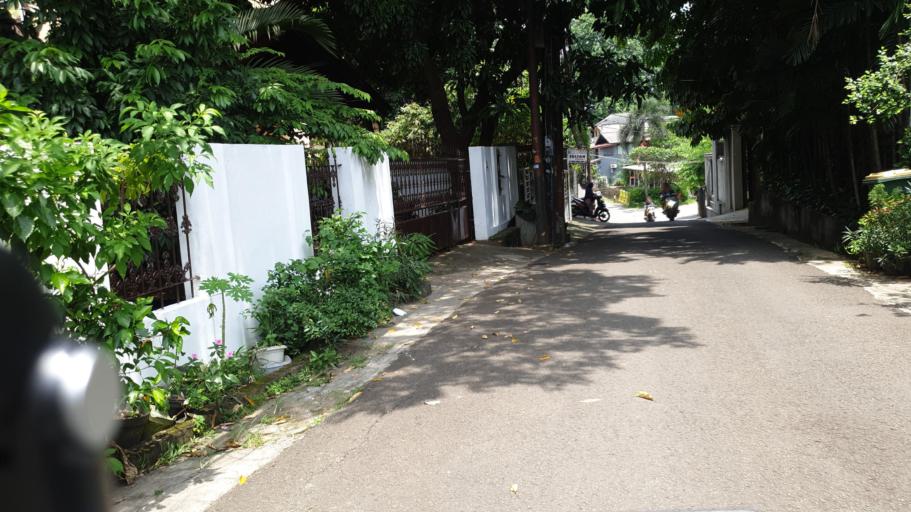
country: ID
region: Banten
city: South Tangerang
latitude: -6.2851
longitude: 106.7910
